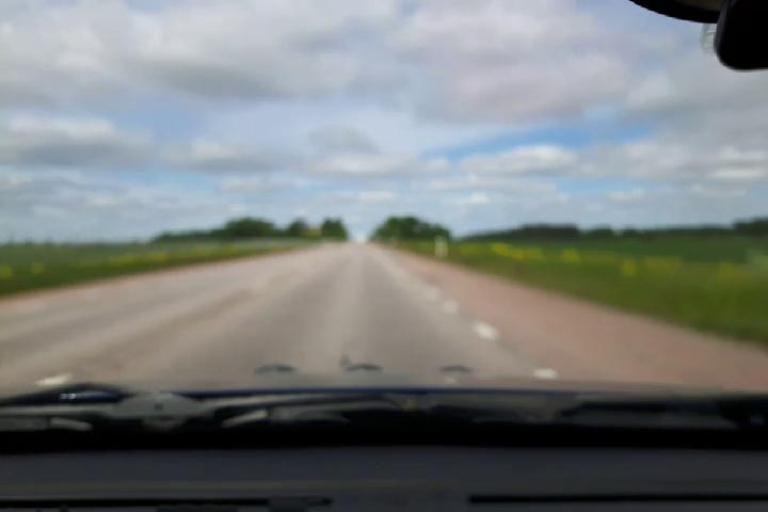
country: SE
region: Uppsala
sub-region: Uppsala Kommun
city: Gamla Uppsala
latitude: 59.9007
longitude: 17.6122
